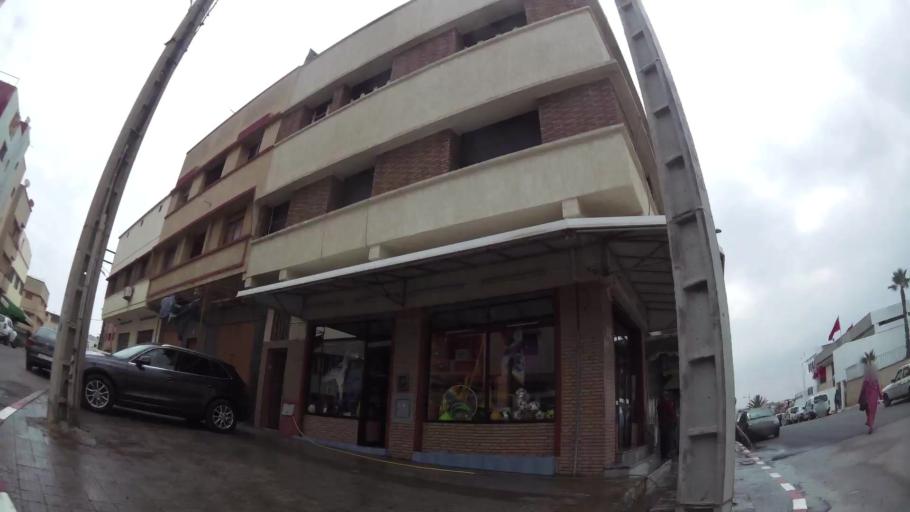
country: MA
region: Rabat-Sale-Zemmour-Zaer
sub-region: Rabat
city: Rabat
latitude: 33.9971
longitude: -6.8720
